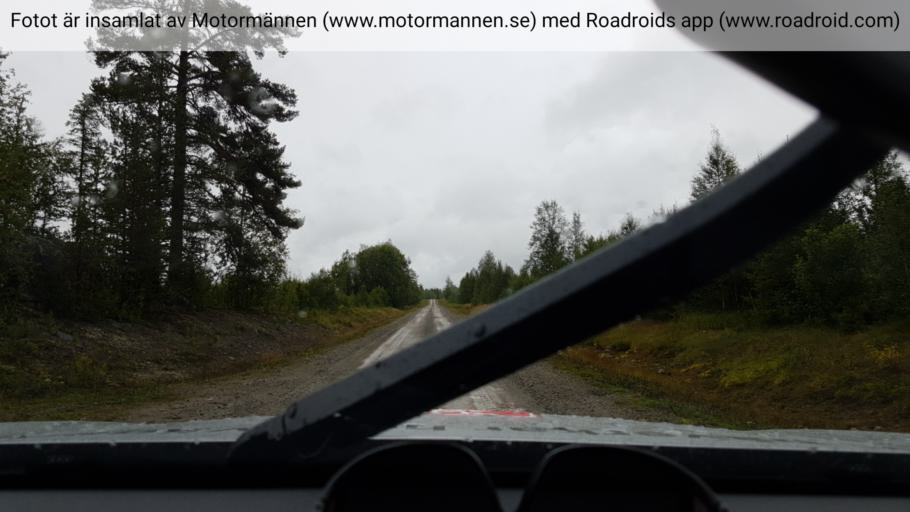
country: SE
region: Vaesterbotten
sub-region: Asele Kommun
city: Insjon
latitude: 64.7862
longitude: 17.5947
